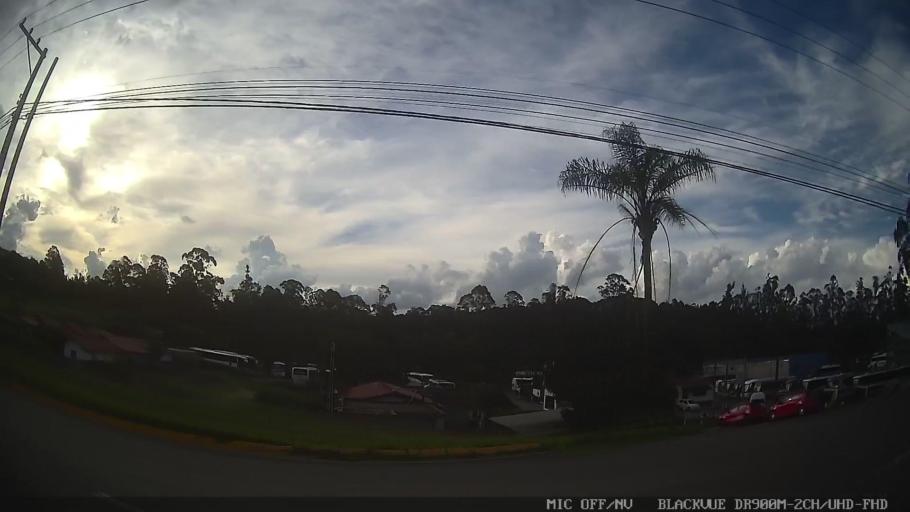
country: BR
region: Minas Gerais
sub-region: Extrema
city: Extrema
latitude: -22.8644
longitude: -46.3353
